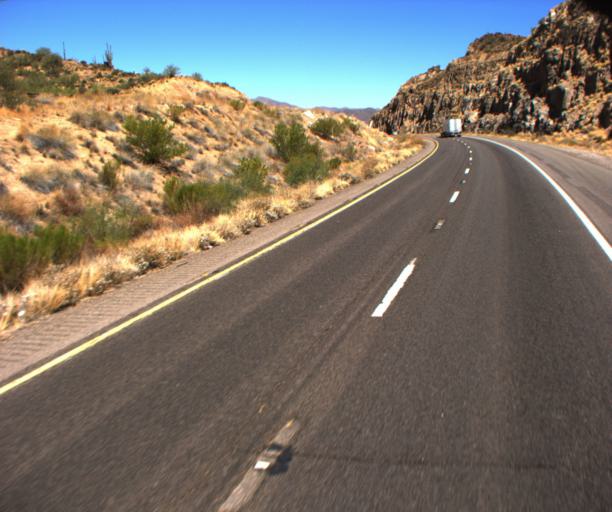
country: US
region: Arizona
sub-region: Maricopa County
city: Rio Verde
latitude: 33.6978
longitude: -111.5015
